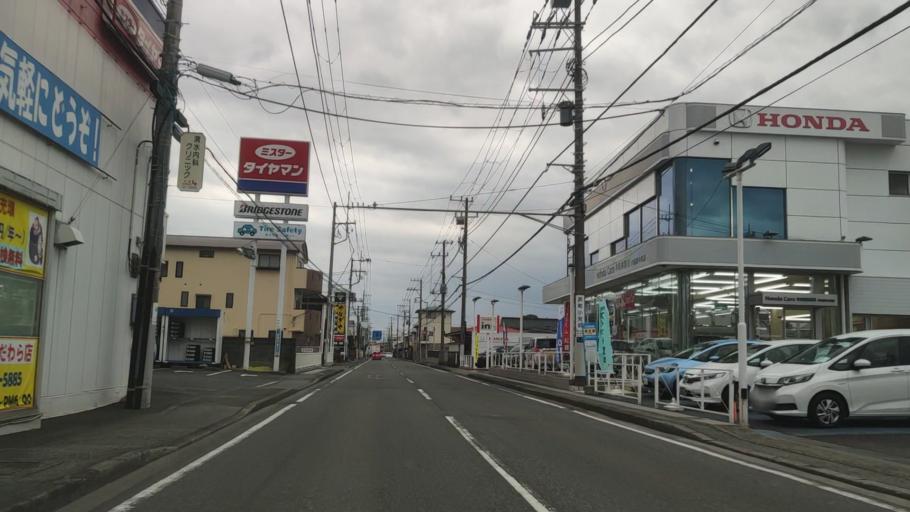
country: JP
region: Kanagawa
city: Odawara
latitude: 35.2663
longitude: 139.1681
